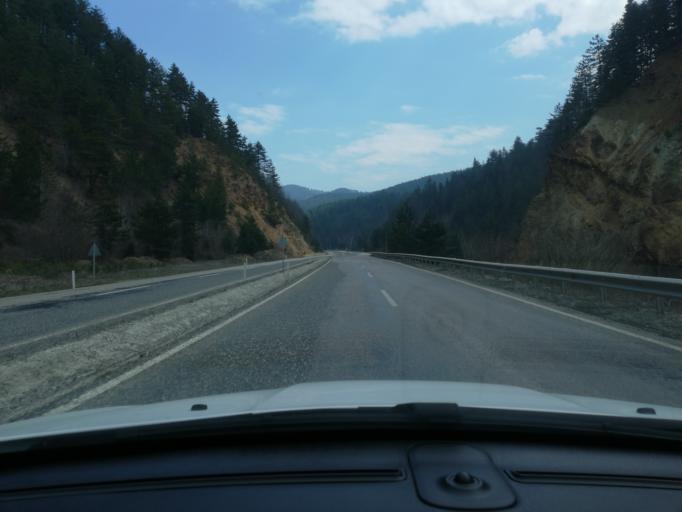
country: TR
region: Kastamonu
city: Kuzyaka
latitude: 41.1539
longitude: 33.7888
